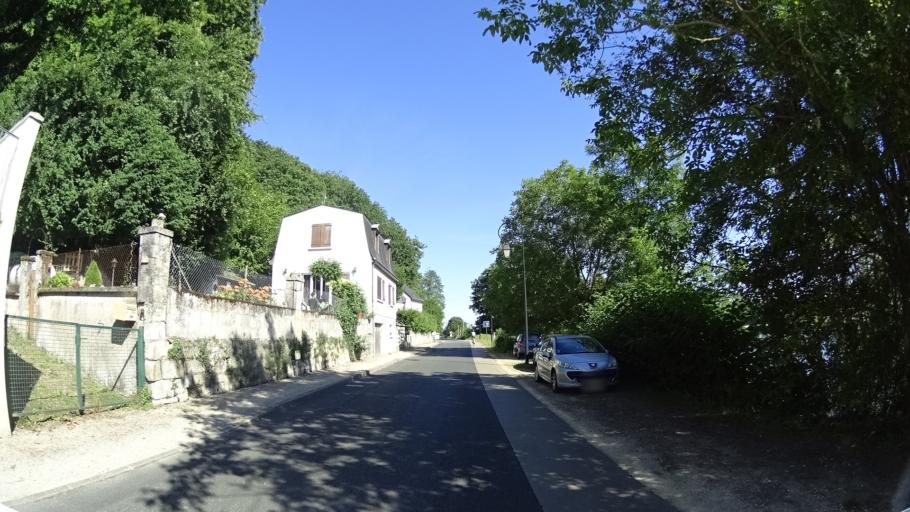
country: FR
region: Pays de la Loire
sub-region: Departement de Maine-et-Loire
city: Saint-Martin-de-la-Place
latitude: 47.3008
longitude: -0.1429
